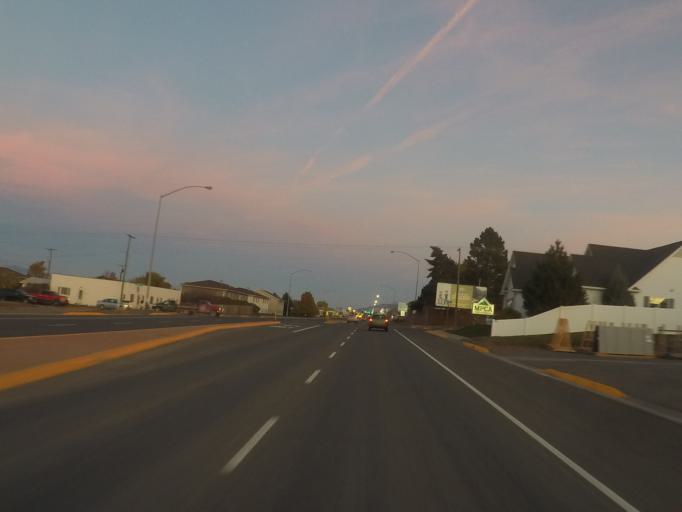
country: US
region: Montana
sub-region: Lewis and Clark County
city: Helena
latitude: 46.6055
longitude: -112.0645
